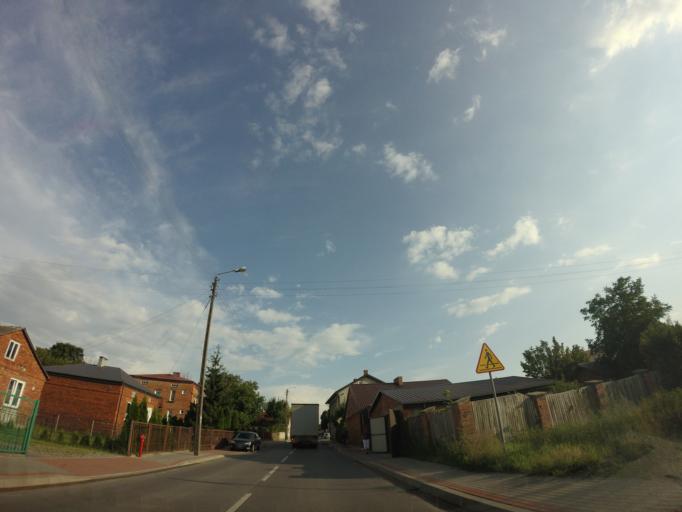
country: PL
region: Lublin Voivodeship
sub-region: Powiat lubartowski
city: Michow
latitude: 51.5248
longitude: 22.3141
